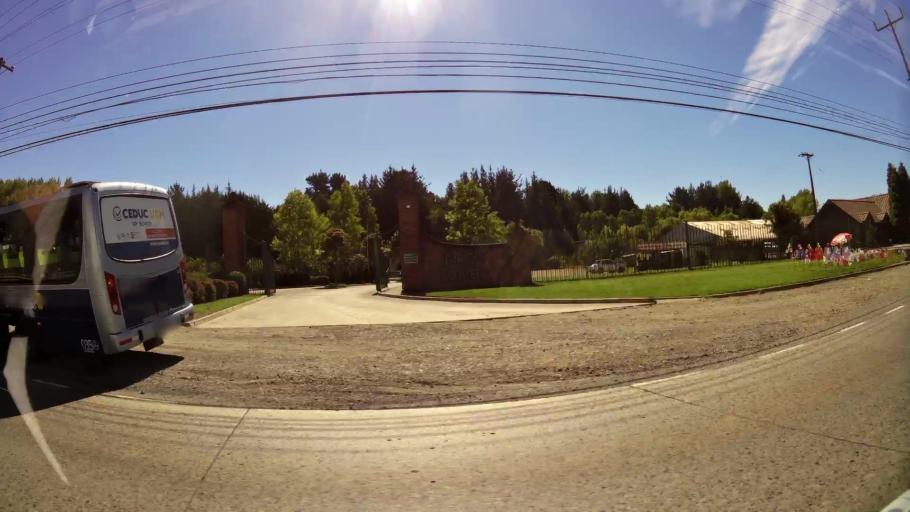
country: CL
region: Biobio
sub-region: Provincia de Concepcion
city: Penco
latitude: -36.7737
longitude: -73.0158
